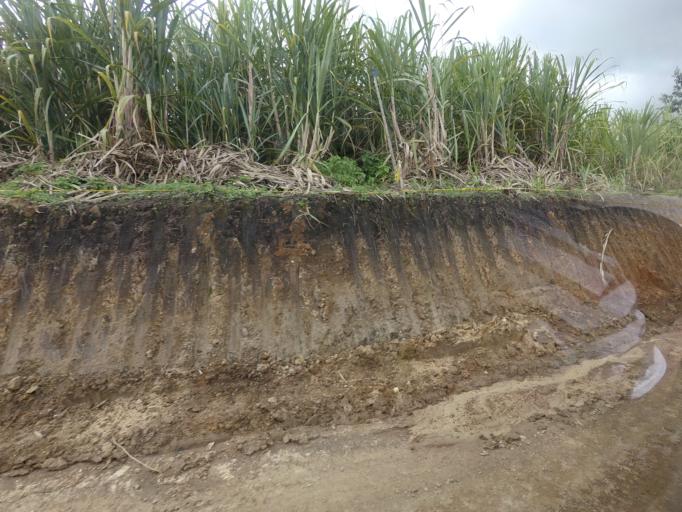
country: CO
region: Huila
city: San Agustin
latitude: 1.9448
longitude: -76.2968
